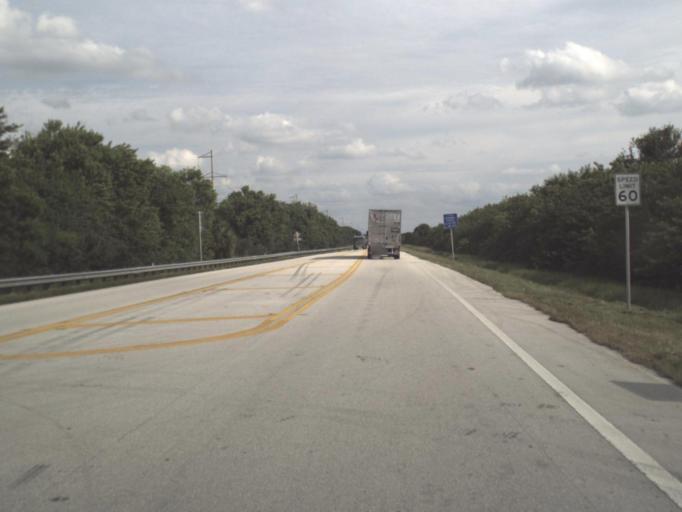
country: US
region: Florida
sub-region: Okeechobee County
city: Taylor Creek
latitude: 27.1591
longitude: -80.6774
